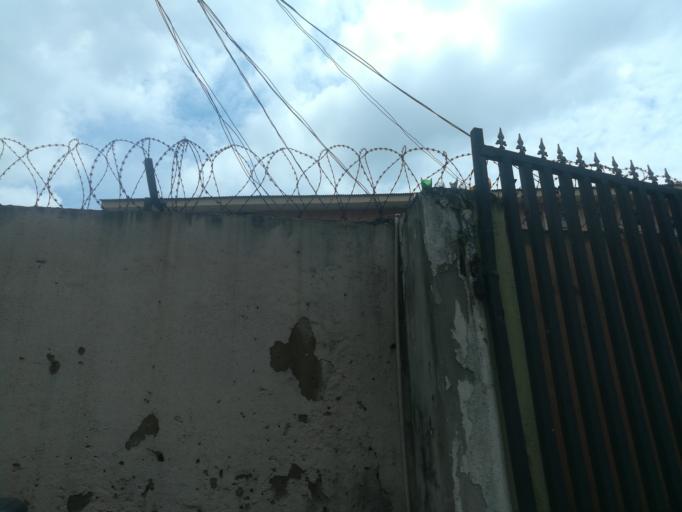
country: NG
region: Lagos
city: Ikeja
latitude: 6.5905
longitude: 3.3600
